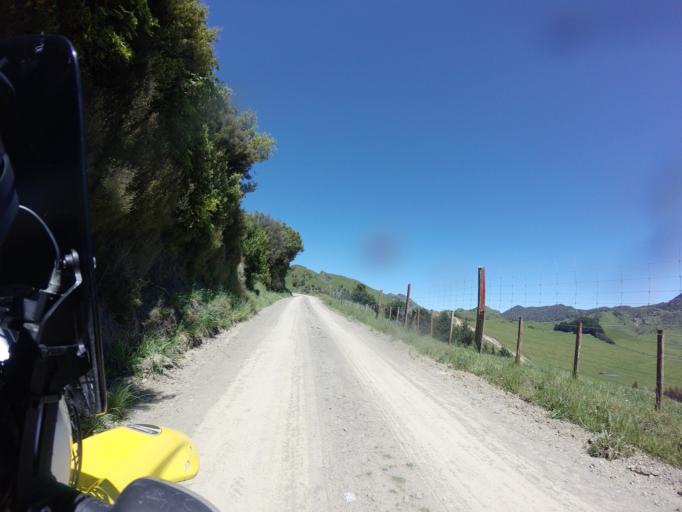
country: NZ
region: Bay of Plenty
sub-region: Opotiki District
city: Opotiki
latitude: -38.4017
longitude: 177.4563
